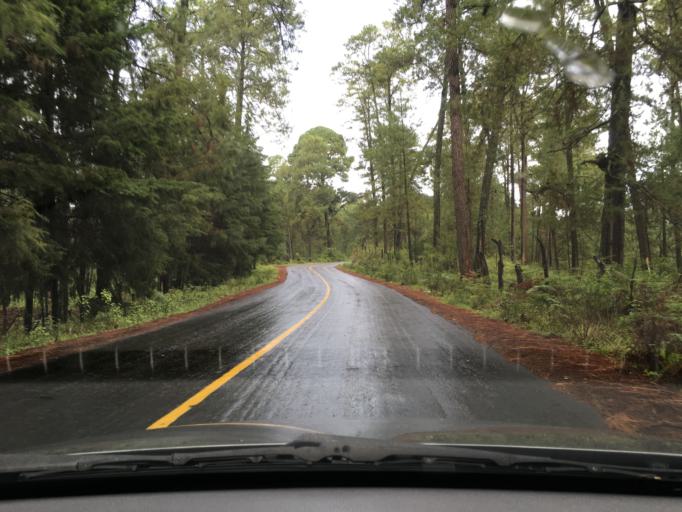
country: MX
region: Michoacan
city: Nuevo San Juan Parangaricutiro
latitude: 19.4408
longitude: -102.1519
